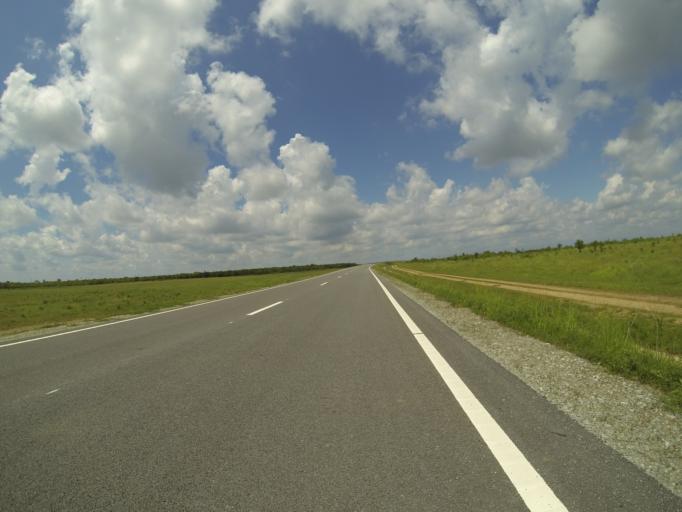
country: RO
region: Dolj
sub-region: Comuna Carcea
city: Carcea
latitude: 44.2812
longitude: 23.9072
